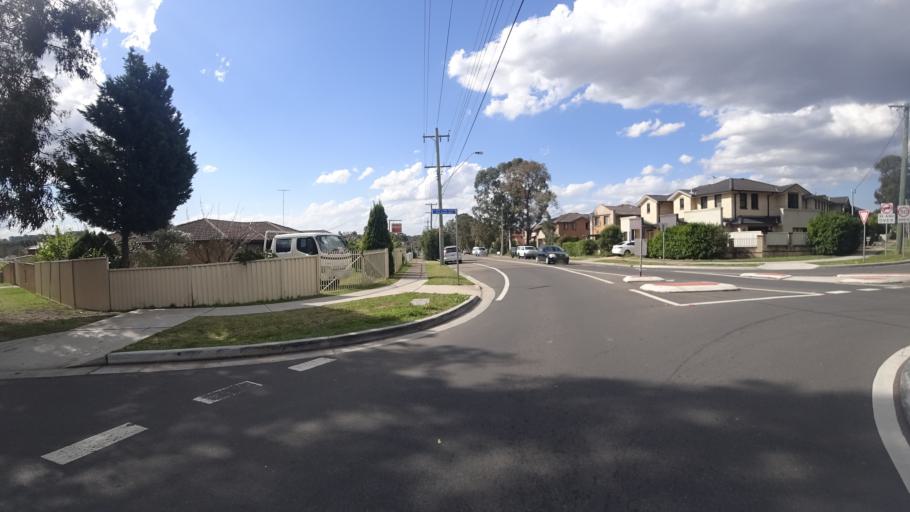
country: AU
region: New South Wales
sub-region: Fairfield
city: Cabramatta West
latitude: -33.9189
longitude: 150.9089
